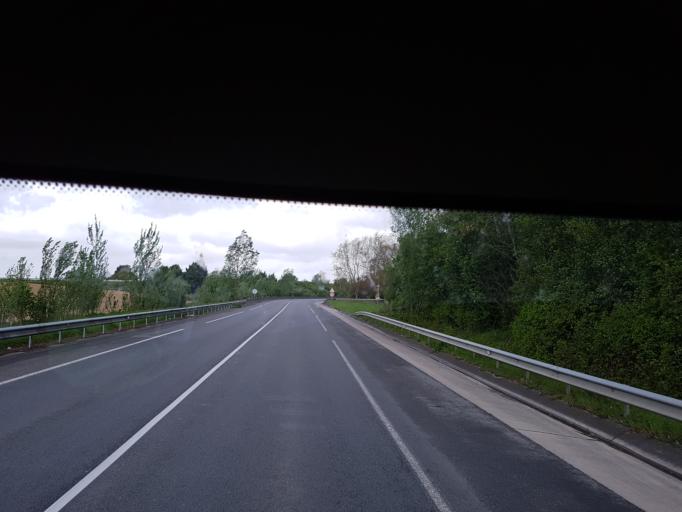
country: FR
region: Nord-Pas-de-Calais
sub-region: Departement du Nord
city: Proville
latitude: 50.1797
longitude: 3.1918
